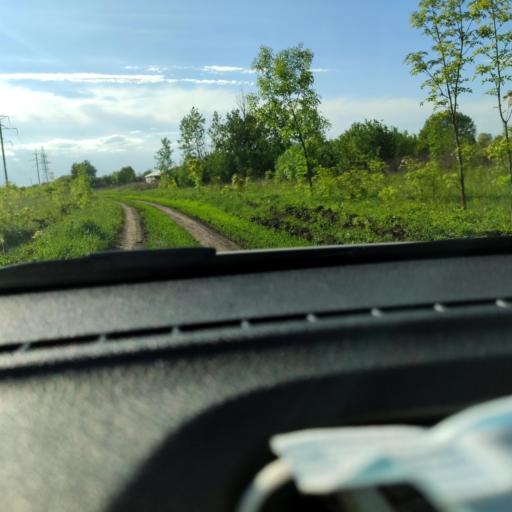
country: RU
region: Voronezj
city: Ramon'
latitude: 51.9486
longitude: 39.3607
